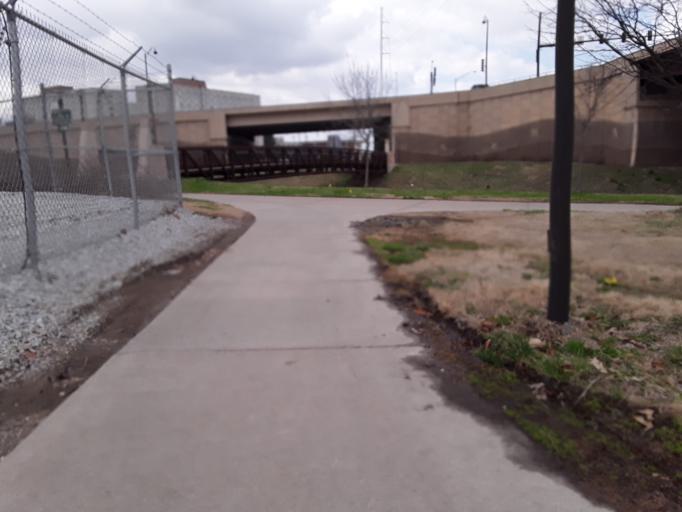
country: US
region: Nebraska
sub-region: Lancaster County
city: Lincoln
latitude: 40.8271
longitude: -96.6973
